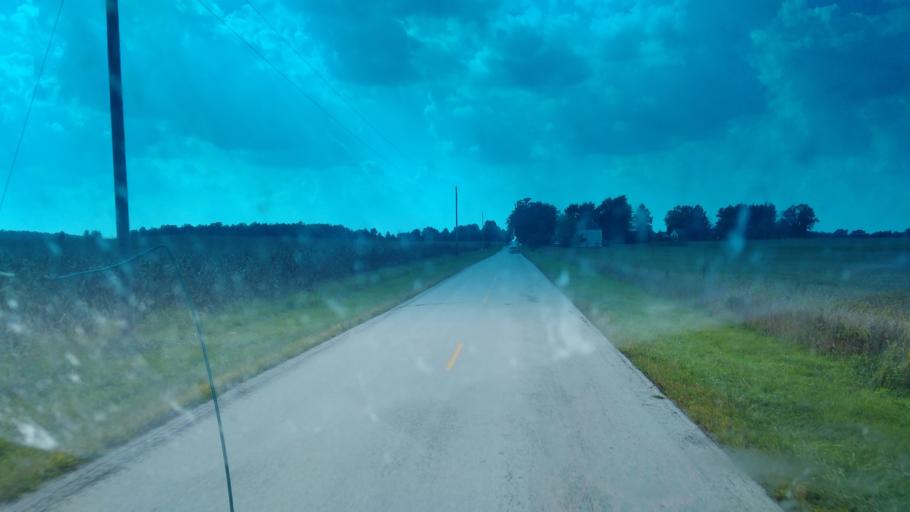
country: US
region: Ohio
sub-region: Hardin County
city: Kenton
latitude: 40.7459
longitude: -83.6077
